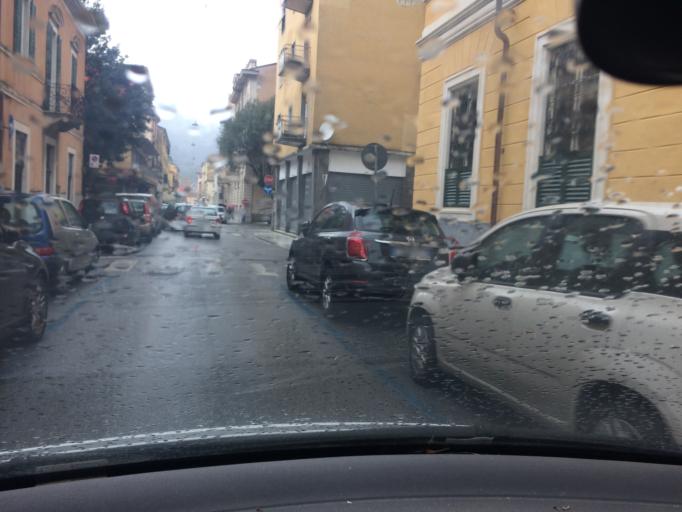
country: IT
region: Tuscany
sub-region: Provincia di Massa-Carrara
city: Carrara
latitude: 44.0761
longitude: 10.1023
